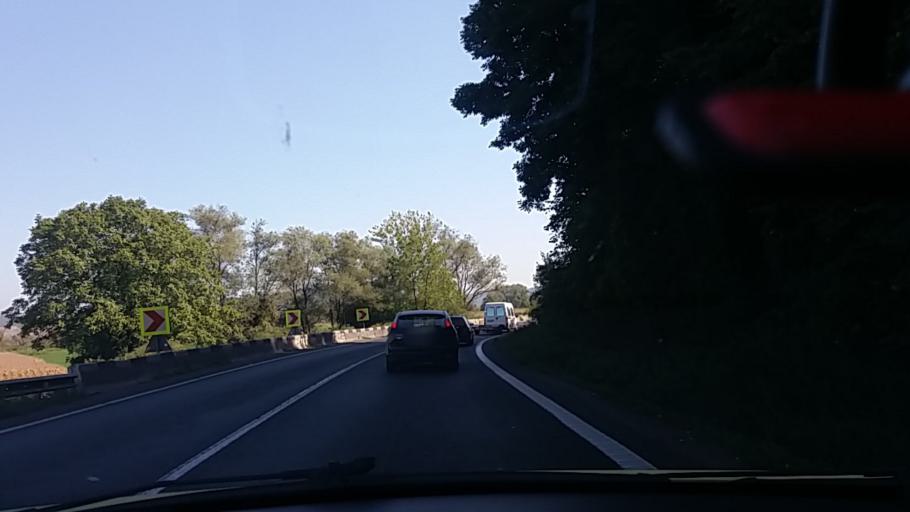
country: RO
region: Hunedoara
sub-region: Comuna Ilia
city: Ilia
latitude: 45.9241
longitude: 22.6980
